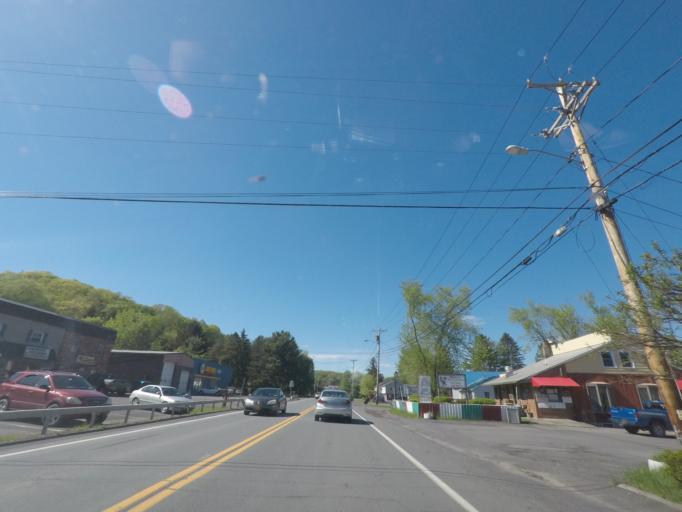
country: US
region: New York
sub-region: Albany County
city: Ravena
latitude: 42.4694
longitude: -73.8165
